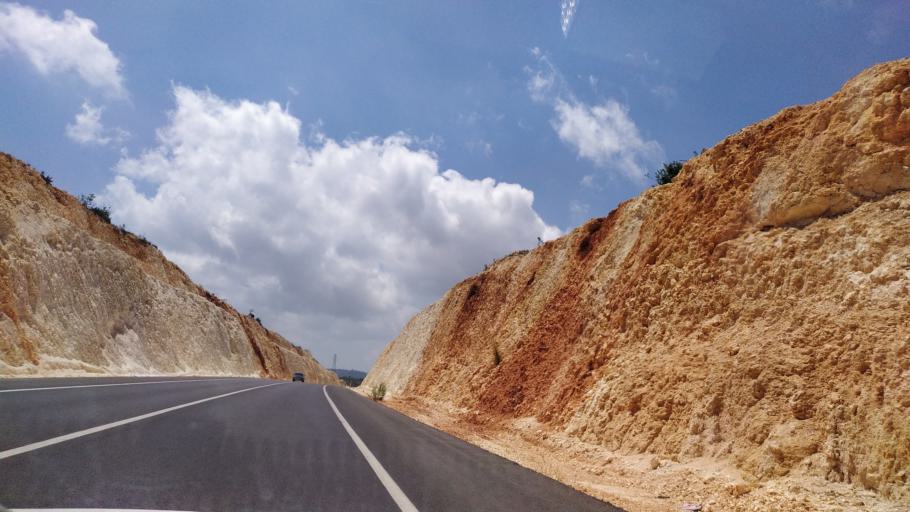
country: TR
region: Mersin
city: Gulnar
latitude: 36.2690
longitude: 33.3709
